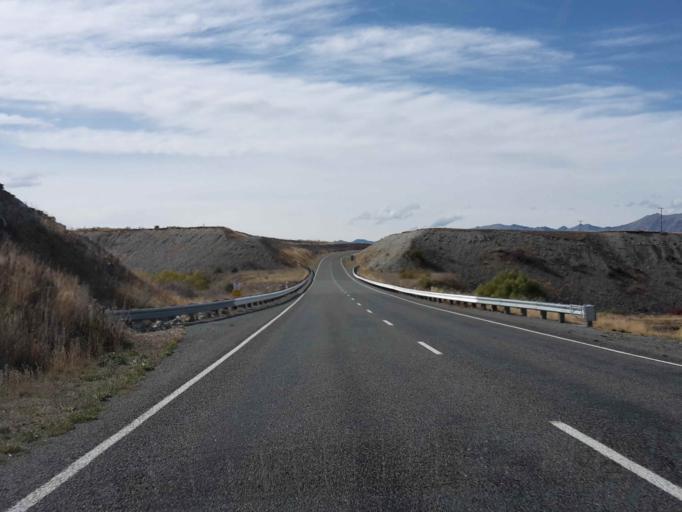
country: NZ
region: Canterbury
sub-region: Timaru District
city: Pleasant Point
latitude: -44.0015
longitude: 170.4108
